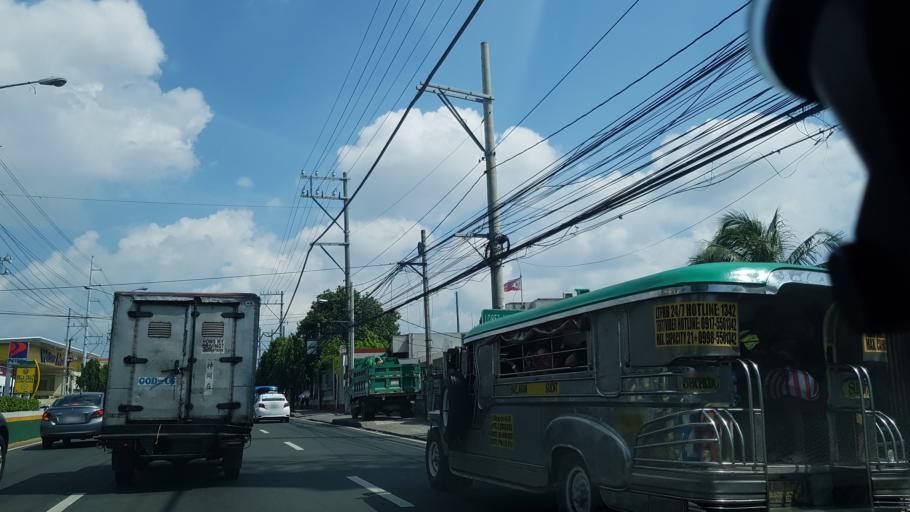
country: PH
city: Sambayanihan People's Village
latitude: 14.4722
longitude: 121.0057
